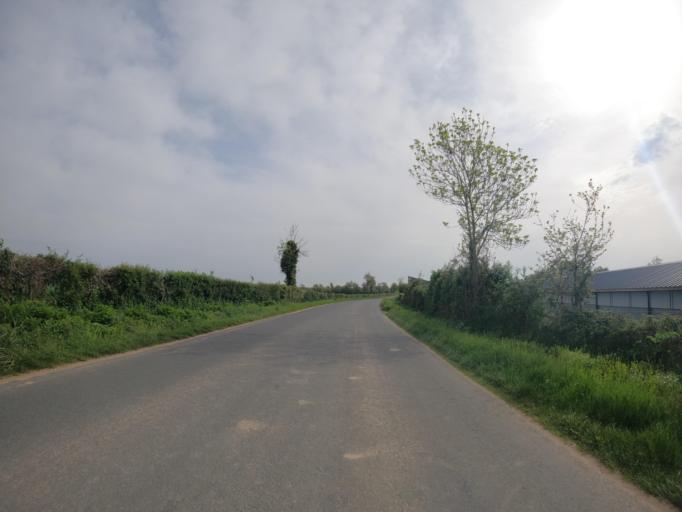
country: FR
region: Poitou-Charentes
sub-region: Departement des Deux-Sevres
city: Moncoutant
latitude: 46.7000
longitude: -0.5337
